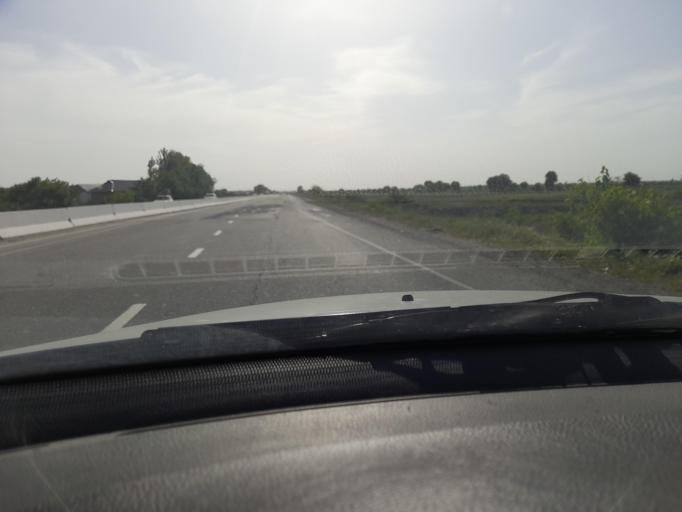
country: UZ
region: Samarqand
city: Kattaqo'rg'on
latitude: 39.9214
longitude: 66.3492
